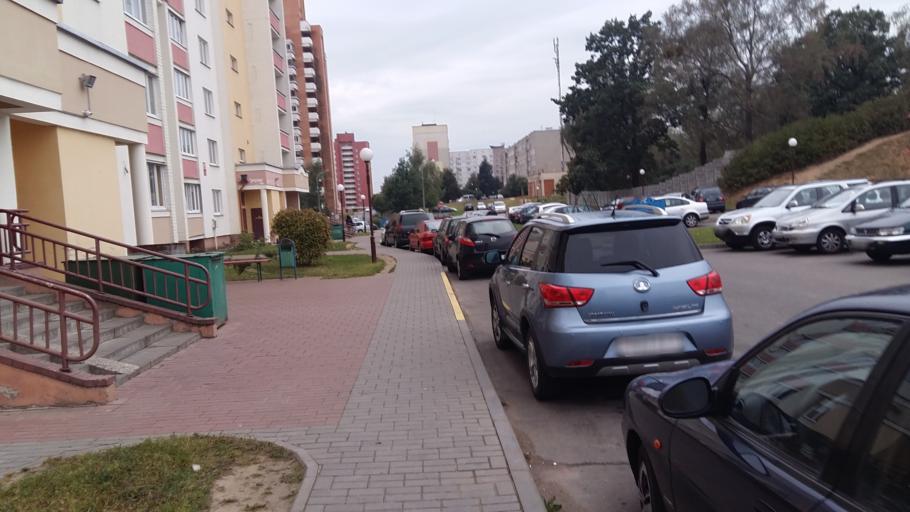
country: BY
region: Grodnenskaya
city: Hrodna
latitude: 53.7107
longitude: 23.8467
